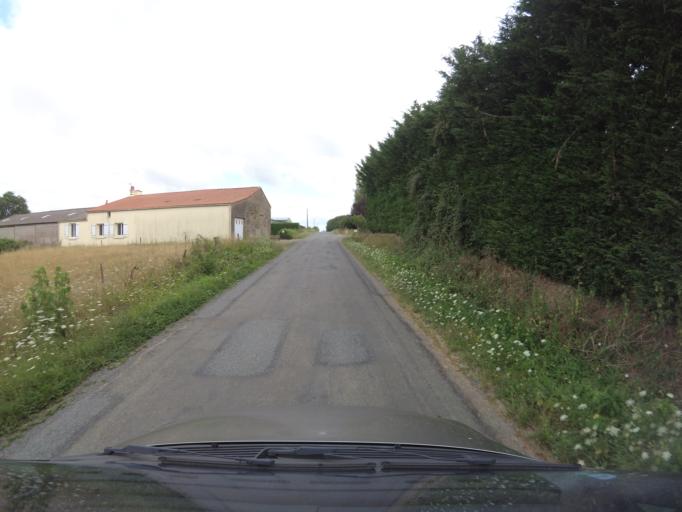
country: FR
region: Pays de la Loire
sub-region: Departement de la Vendee
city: Saint-Philbert-de-Bouaine
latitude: 47.0133
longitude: -1.5490
